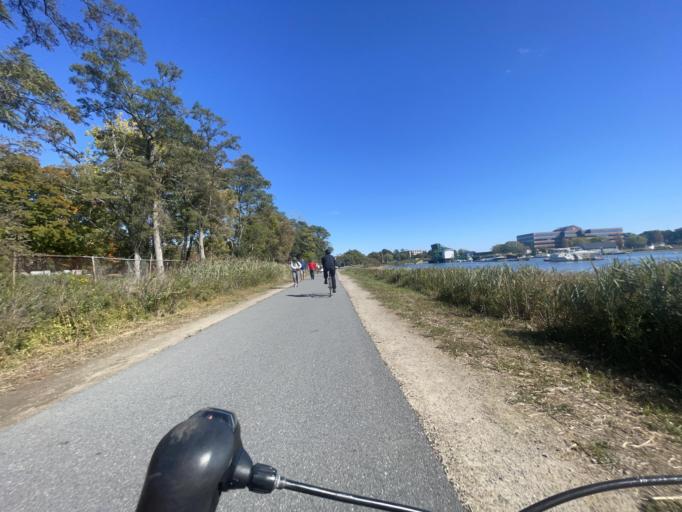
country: US
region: Massachusetts
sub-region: Norfolk County
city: Milton
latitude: 42.2769
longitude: -71.0558
